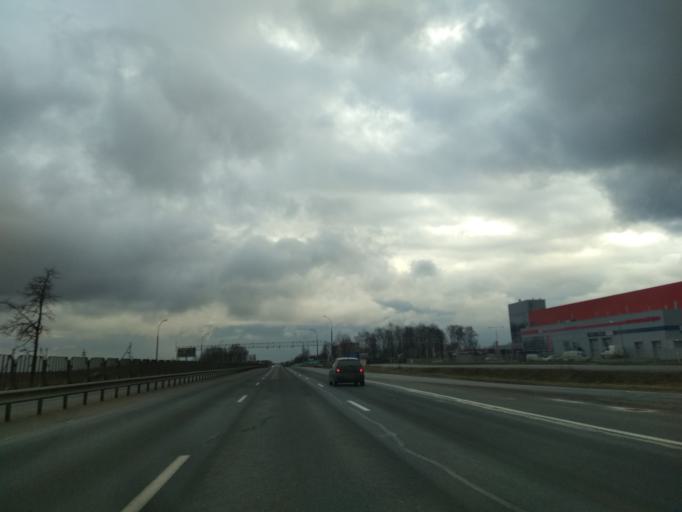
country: BY
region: Minsk
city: Pryvol'ny
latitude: 53.8030
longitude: 27.7972
